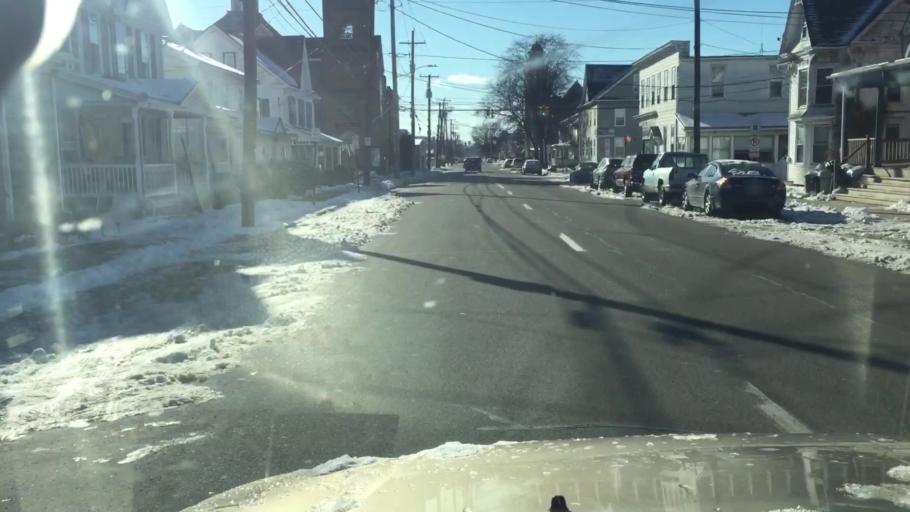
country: US
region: Pennsylvania
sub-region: Columbia County
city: Berwick
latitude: 41.0565
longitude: -76.2316
